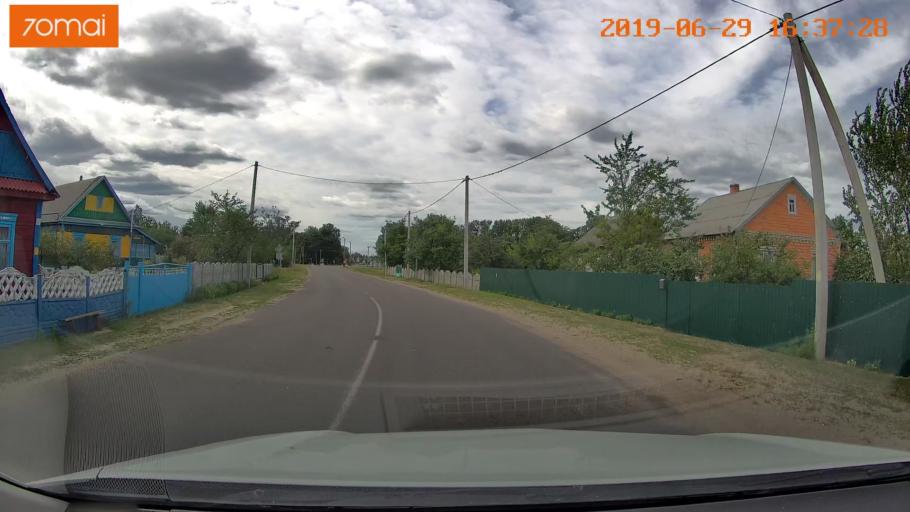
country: BY
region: Brest
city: Luninyets
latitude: 52.2278
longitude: 27.0215
